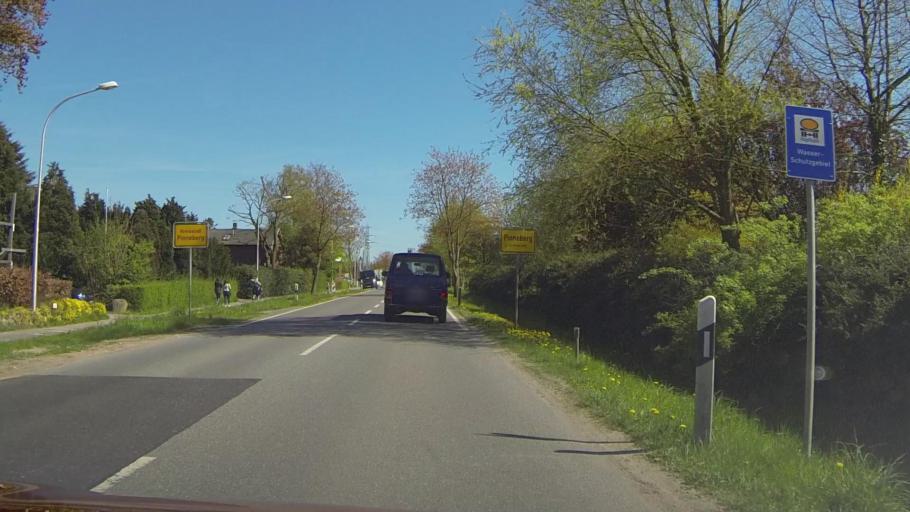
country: DE
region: Schleswig-Holstein
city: Kummerfeld
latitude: 53.6717
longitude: 9.7758
